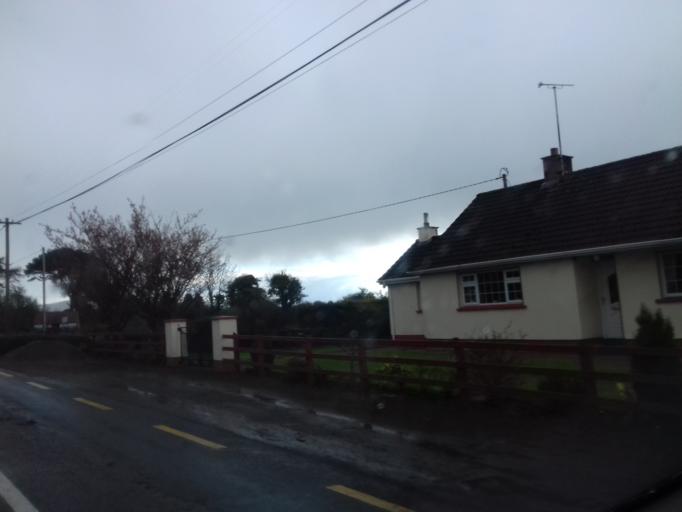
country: IE
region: Connaught
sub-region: County Leitrim
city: Manorhamilton
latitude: 54.2654
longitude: -7.9422
